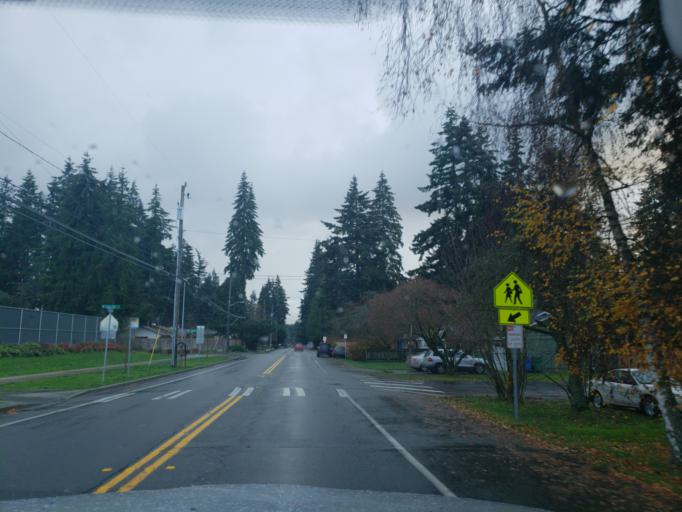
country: US
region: Washington
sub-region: King County
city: Shoreline
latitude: 47.7531
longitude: -122.3510
